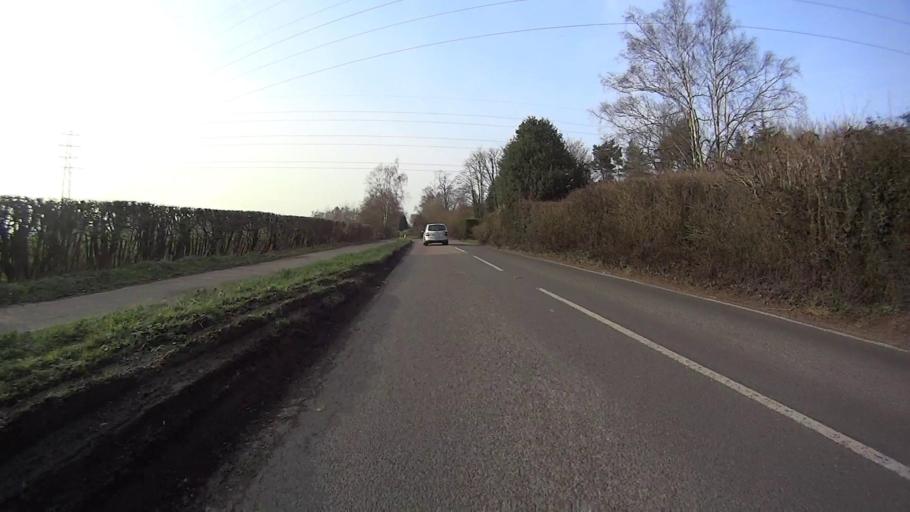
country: GB
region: England
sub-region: West Sussex
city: Copthorne
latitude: 51.1138
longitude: -0.1233
